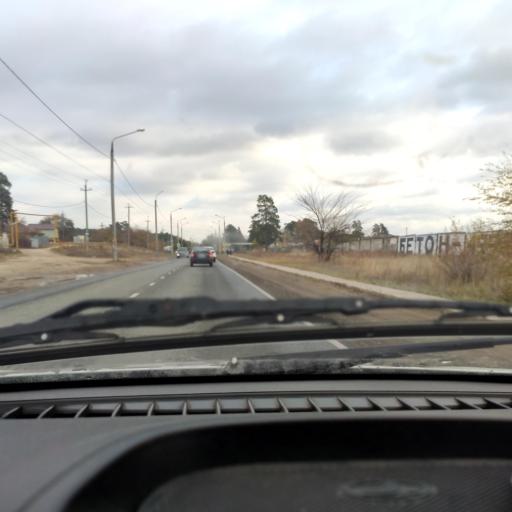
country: RU
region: Samara
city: Zhigulevsk
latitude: 53.4647
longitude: 49.5969
